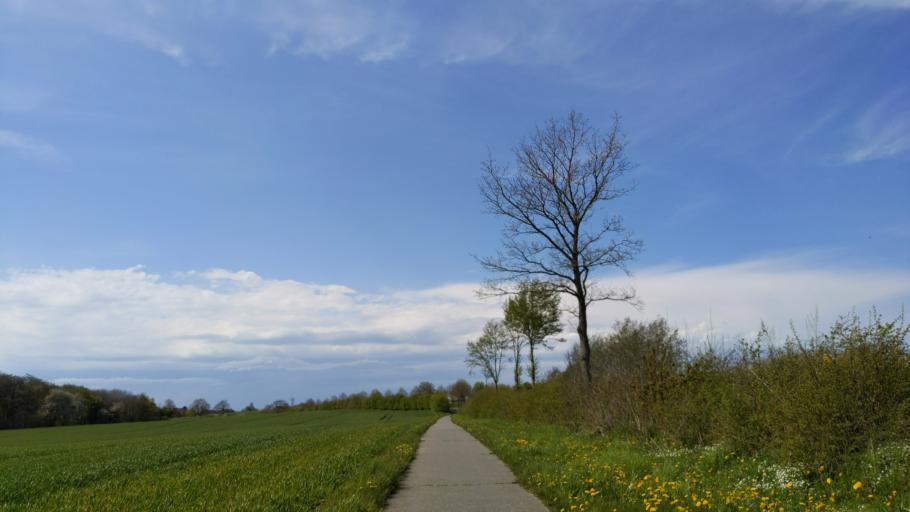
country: DE
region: Schleswig-Holstein
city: Stockelsdorf
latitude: 53.9224
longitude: 10.6587
